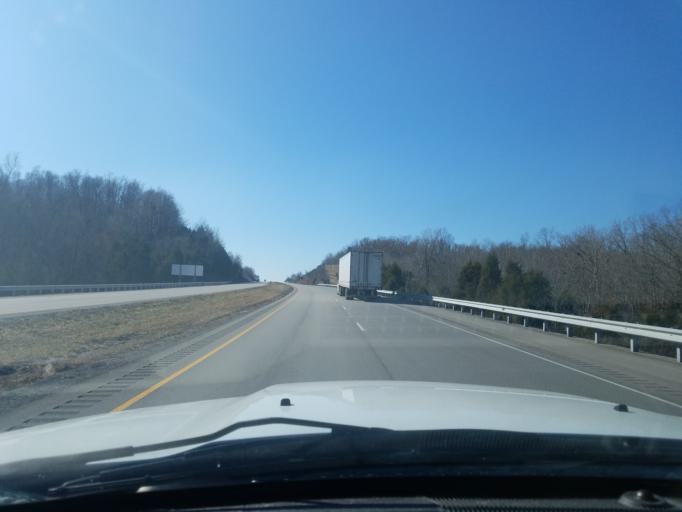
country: US
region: Kentucky
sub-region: Grayson County
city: Leitchfield
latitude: 37.4646
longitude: -86.3001
